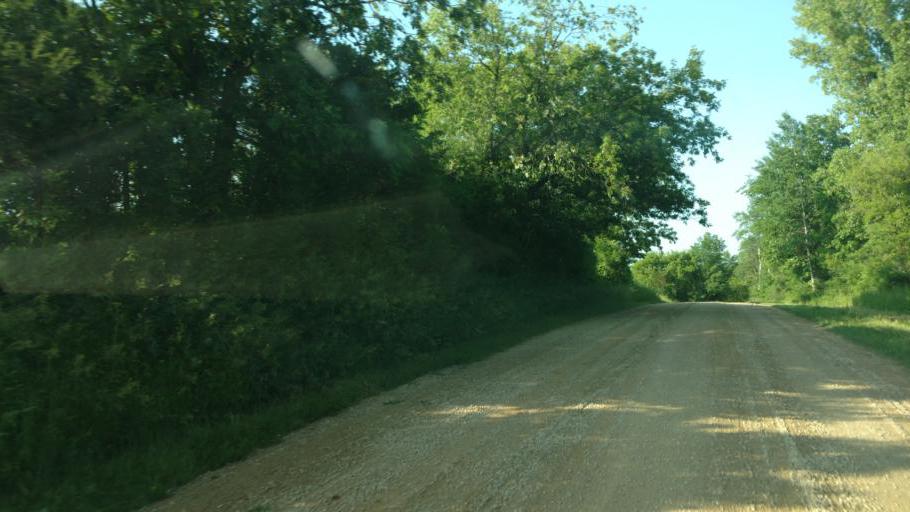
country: US
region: Wisconsin
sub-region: Vernon County
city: Hillsboro
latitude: 43.6329
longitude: -90.3546
